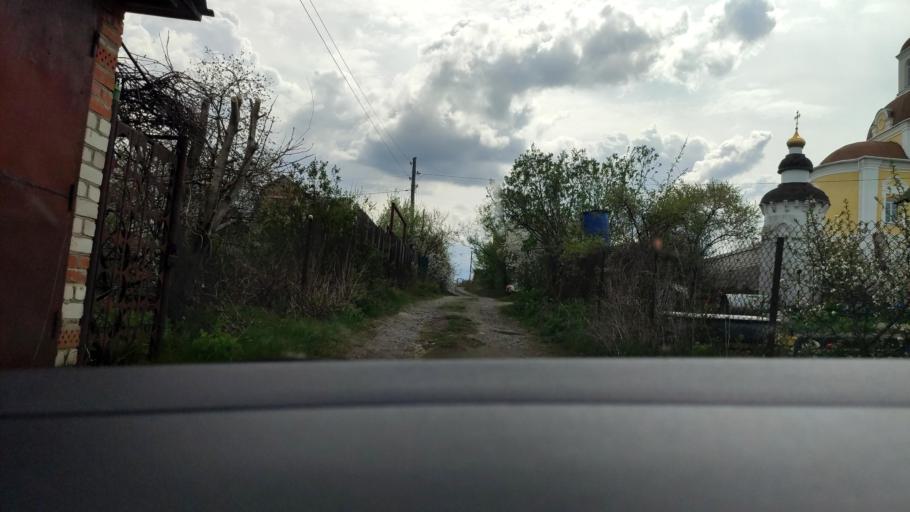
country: RU
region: Voronezj
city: Semiluki
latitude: 51.7810
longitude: 38.9993
